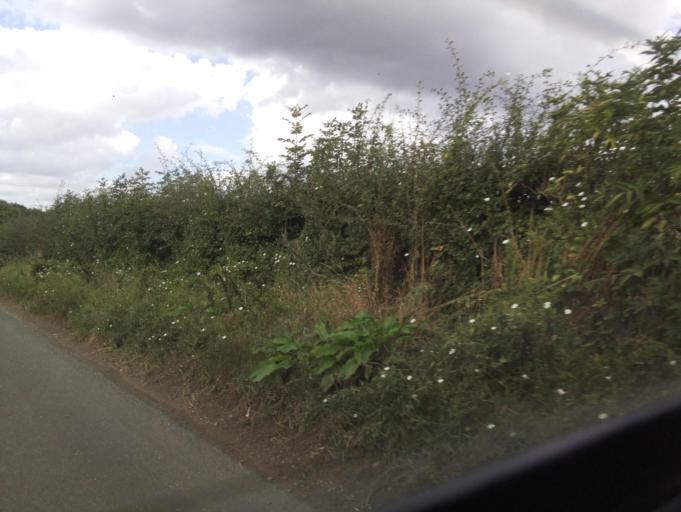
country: GB
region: England
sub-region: North Yorkshire
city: Bedale
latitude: 54.2256
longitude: -1.6407
